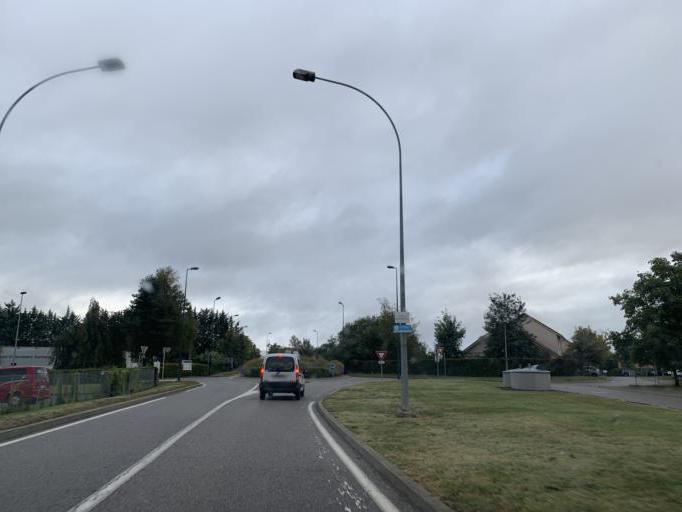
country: FR
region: Rhone-Alpes
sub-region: Departement de l'Ain
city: Belley
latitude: 45.7443
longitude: 5.6811
